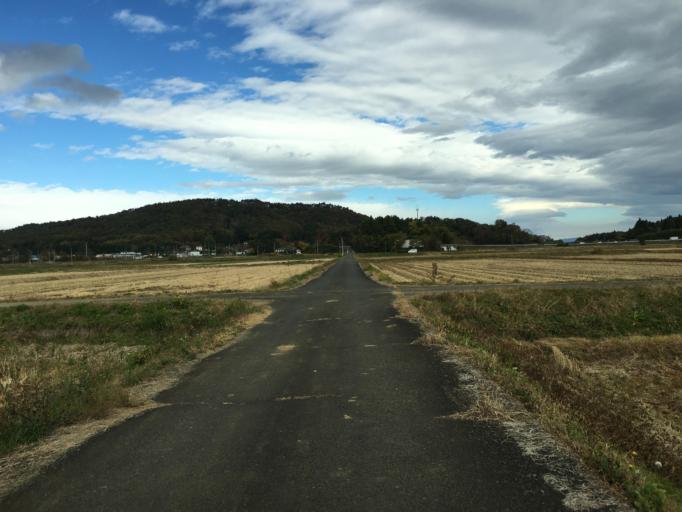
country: JP
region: Fukushima
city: Nihommatsu
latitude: 37.6562
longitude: 140.4476
